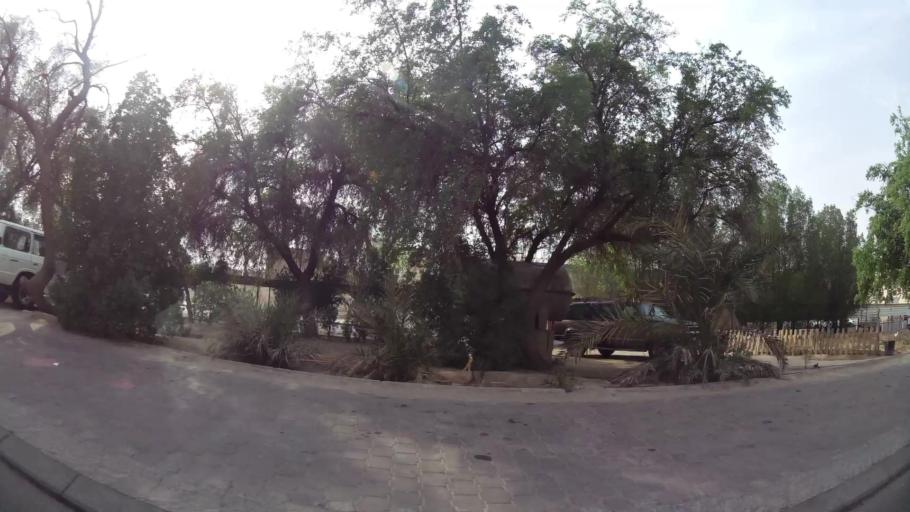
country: KW
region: Al Farwaniyah
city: Al Farwaniyah
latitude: 29.2933
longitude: 47.9626
